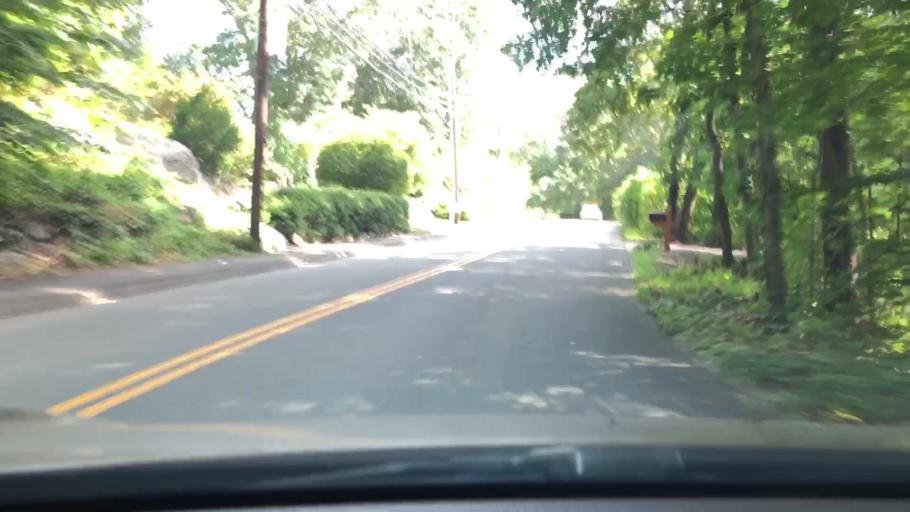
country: US
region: Connecticut
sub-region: Fairfield County
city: Darien
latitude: 41.1085
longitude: -73.4454
